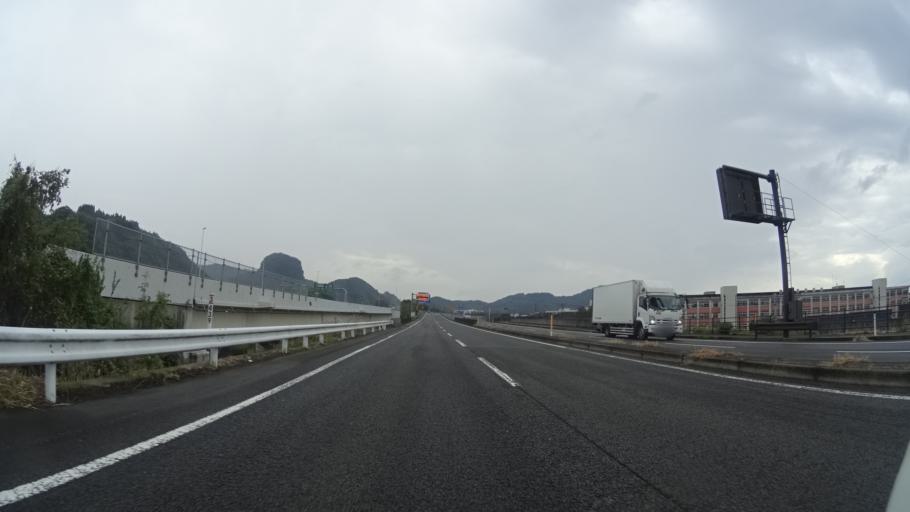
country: JP
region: Kagoshima
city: Kajiki
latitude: 31.7489
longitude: 130.6634
